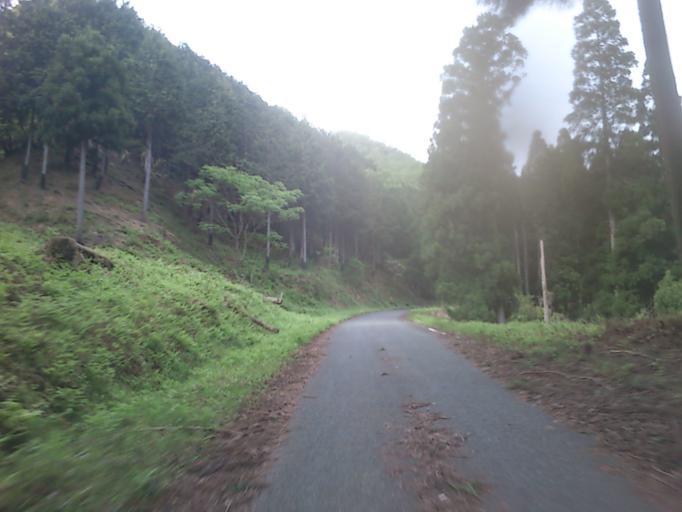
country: JP
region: Hyogo
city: Toyooka
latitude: 35.6100
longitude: 134.9910
